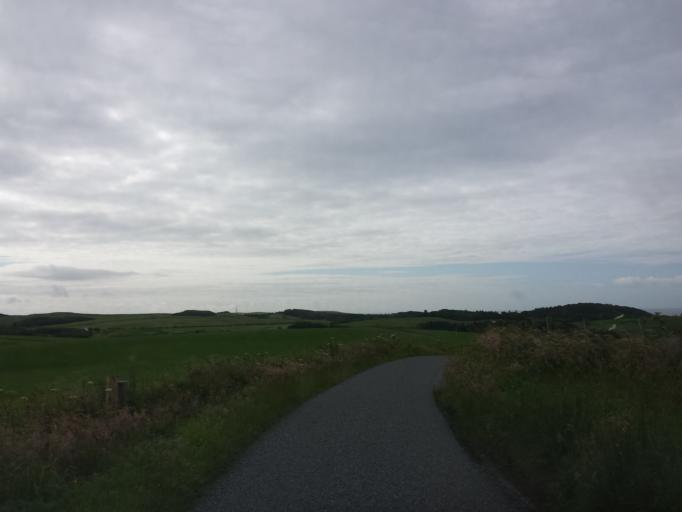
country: GB
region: Scotland
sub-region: Dumfries and Galloway
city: Stranraer
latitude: 54.8773
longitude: -5.1188
